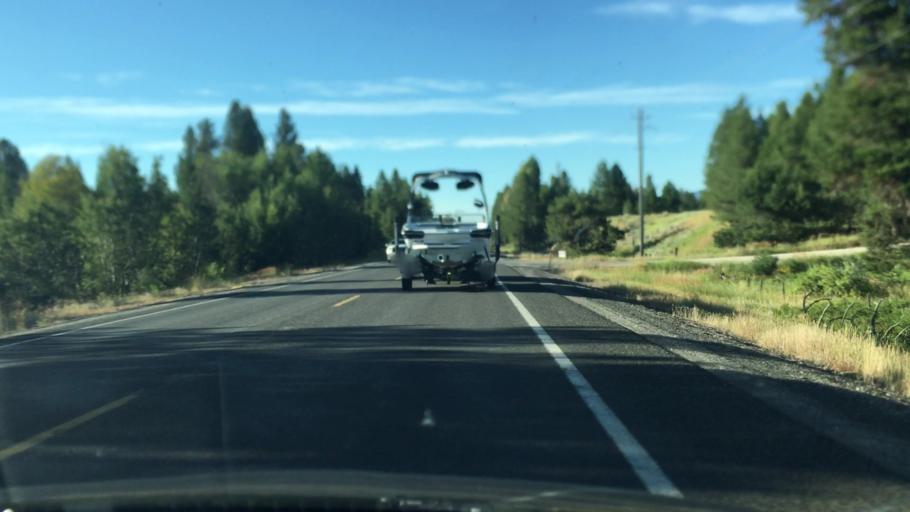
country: US
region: Idaho
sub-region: Valley County
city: Cascade
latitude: 44.4628
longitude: -115.9992
